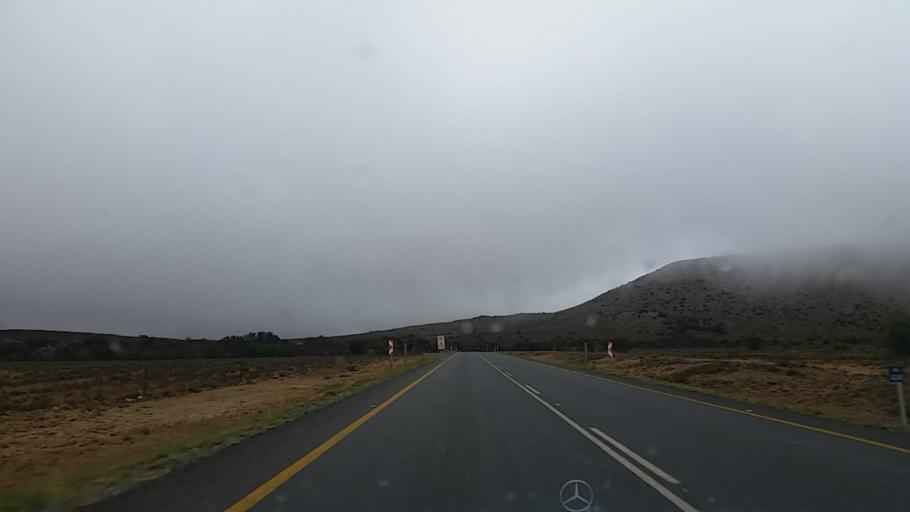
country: ZA
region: Eastern Cape
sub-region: Cacadu District Municipality
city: Graaff-Reinet
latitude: -31.9430
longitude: 24.7302
